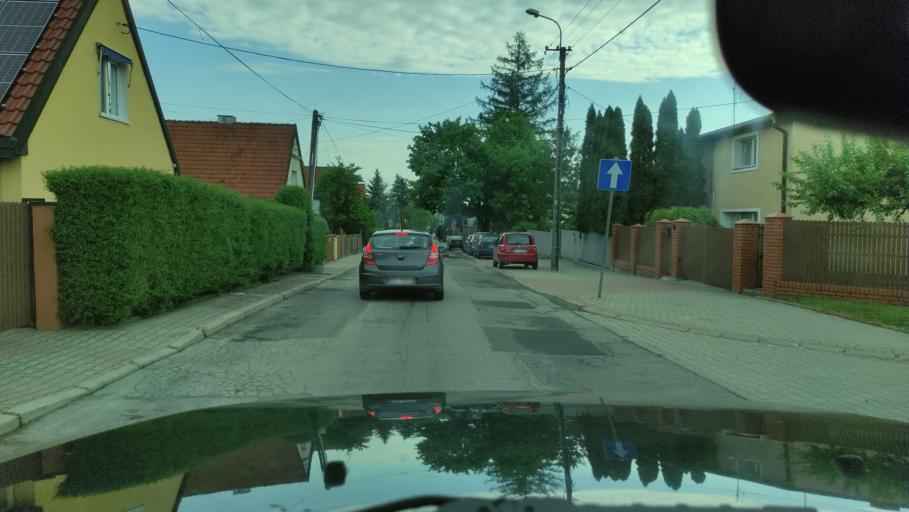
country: PL
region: Warmian-Masurian Voivodeship
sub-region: Powiat olsztynski
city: Olsztyn
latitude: 53.7635
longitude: 20.5073
